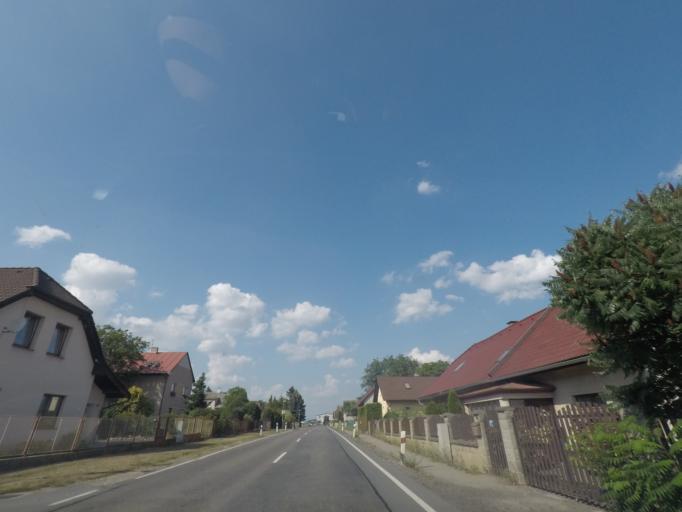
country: CZ
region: Kralovehradecky
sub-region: Okres Nachod
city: Jaromer
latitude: 50.3229
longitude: 15.9500
